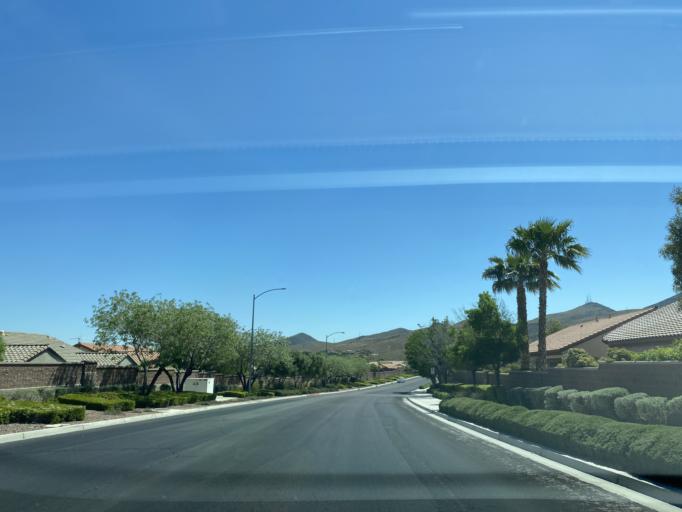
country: US
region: Nevada
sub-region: Clark County
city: Whitney
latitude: 35.9531
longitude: -115.0892
